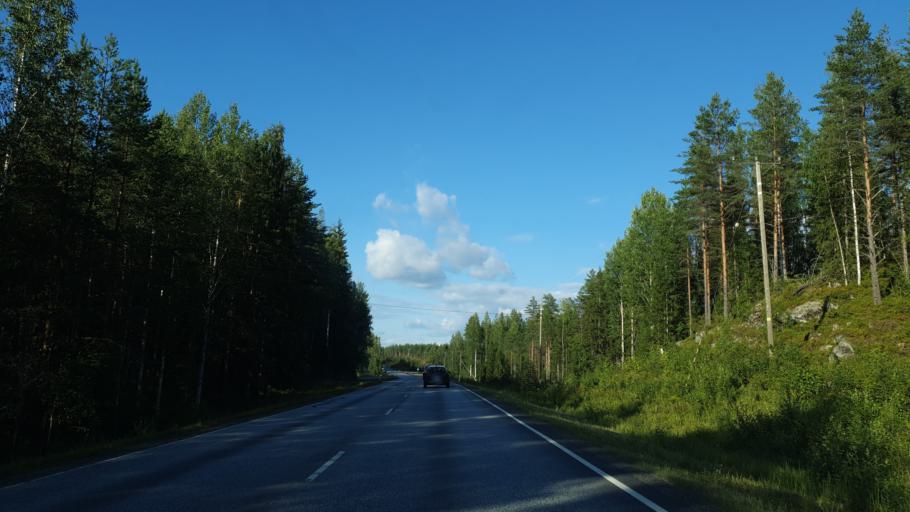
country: FI
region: North Karelia
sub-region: Joensuu
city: Outokumpu
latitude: 62.5391
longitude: 29.1196
